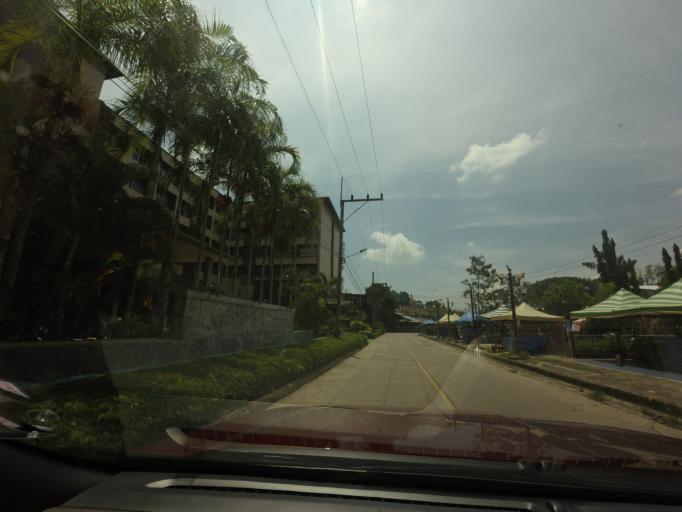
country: TH
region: Yala
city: Betong
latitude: 5.7689
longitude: 101.0740
